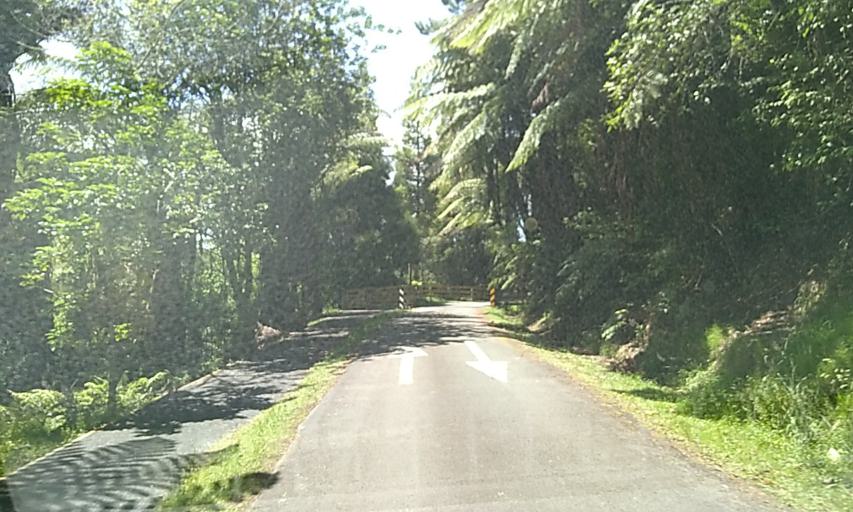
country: NZ
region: Bay of Plenty
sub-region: Tauranga City
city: Tauranga
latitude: -37.8183
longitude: 176.0390
